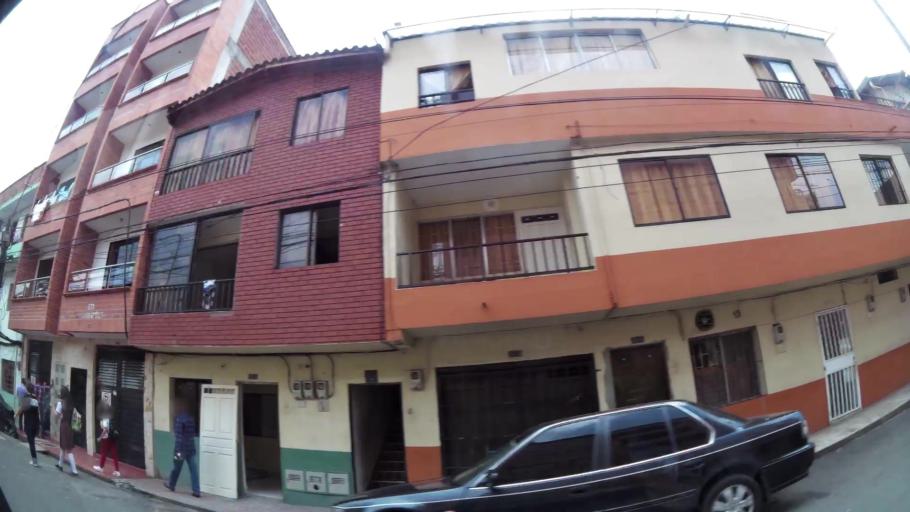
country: CO
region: Antioquia
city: Envigado
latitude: 6.1704
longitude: -75.6069
